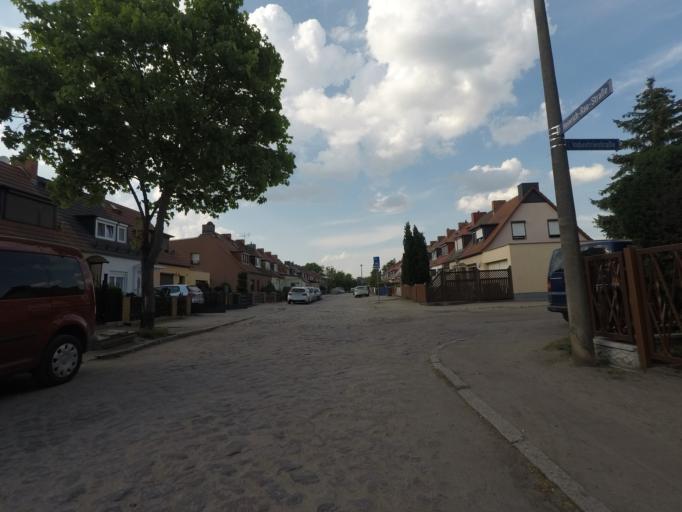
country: DE
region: Brandenburg
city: Melchow
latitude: 52.8426
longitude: 13.7185
